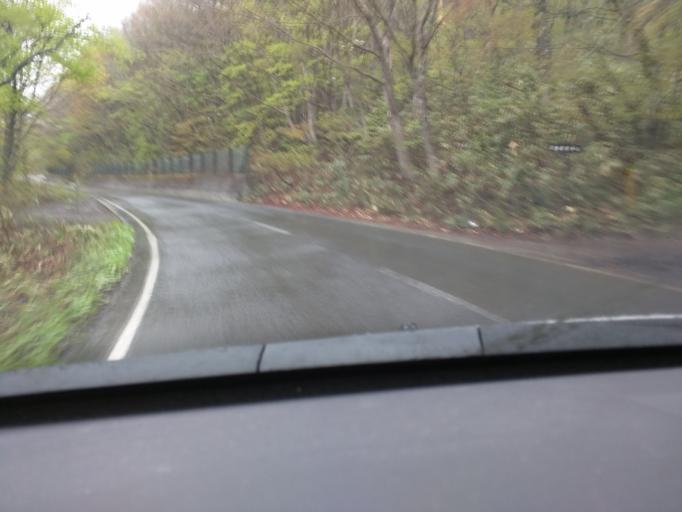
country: JP
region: Fukushima
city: Inawashiro
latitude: 37.6533
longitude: 140.2536
